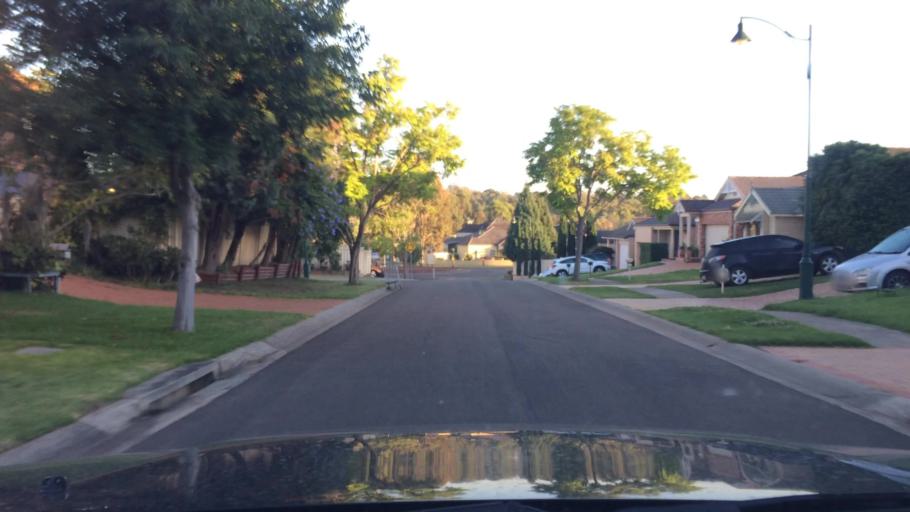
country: AU
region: New South Wales
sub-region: Campbelltown Municipality
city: Denham Court
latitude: -33.9371
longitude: 150.8336
